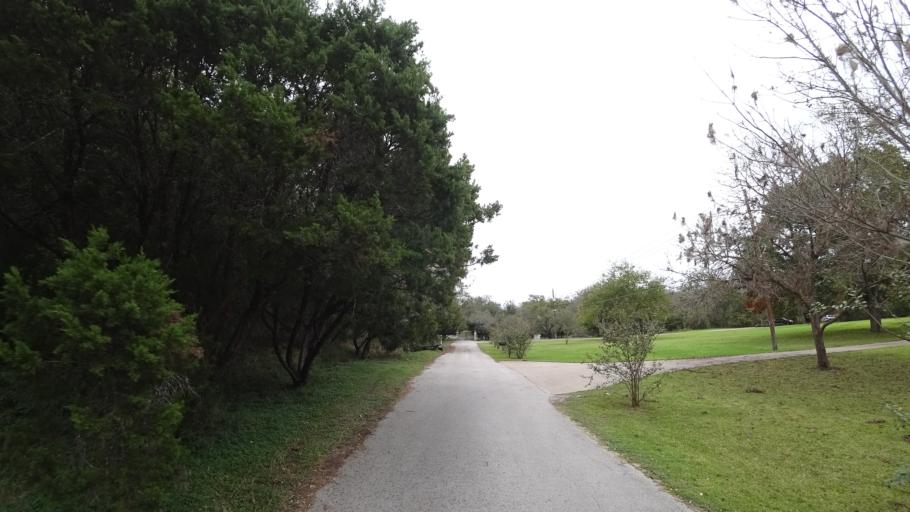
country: US
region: Texas
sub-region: Travis County
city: Bee Cave
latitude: 30.3447
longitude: -97.9294
